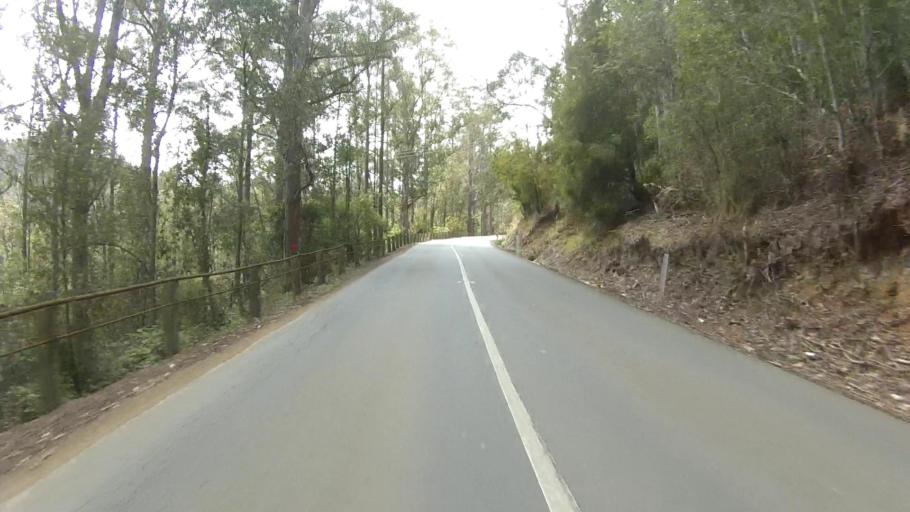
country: AU
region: Tasmania
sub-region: Kingborough
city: Kettering
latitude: -43.1271
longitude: 147.1806
